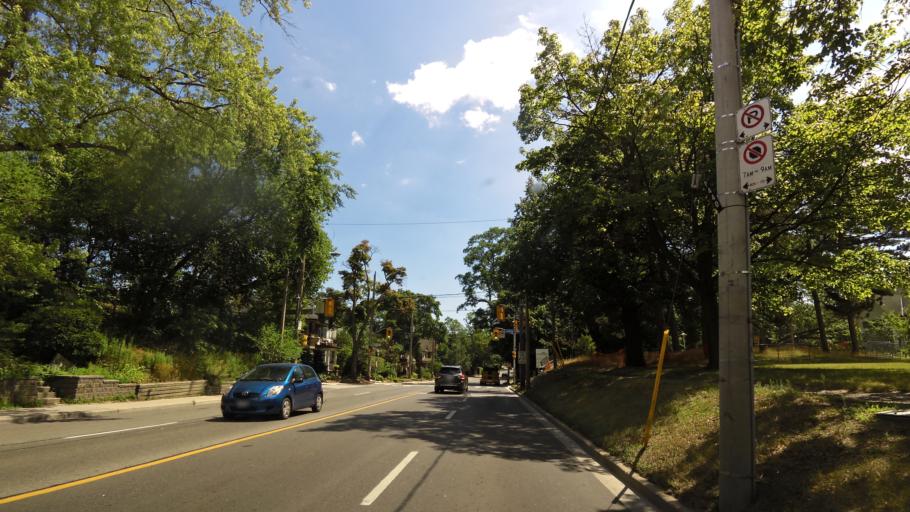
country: CA
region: Ontario
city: Toronto
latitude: 43.6516
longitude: -79.4587
